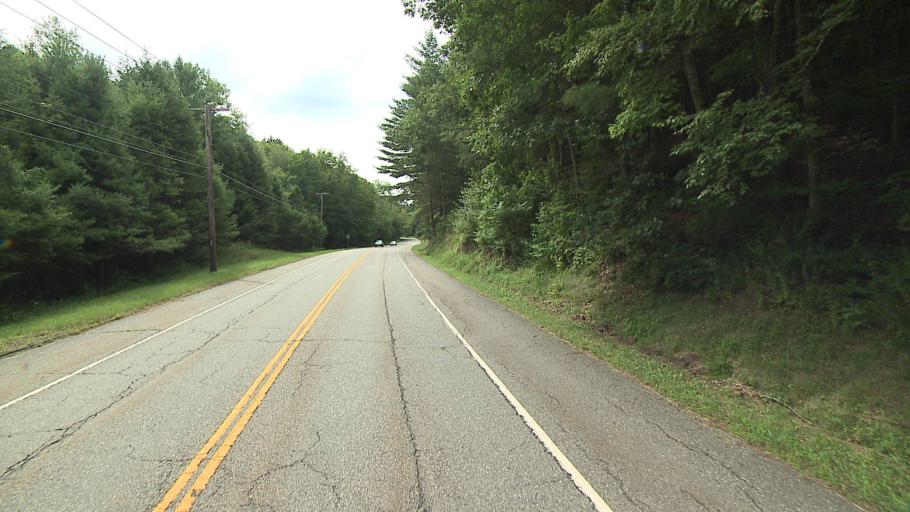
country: US
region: Connecticut
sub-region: Litchfield County
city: New Preston
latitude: 41.6631
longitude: -73.3206
